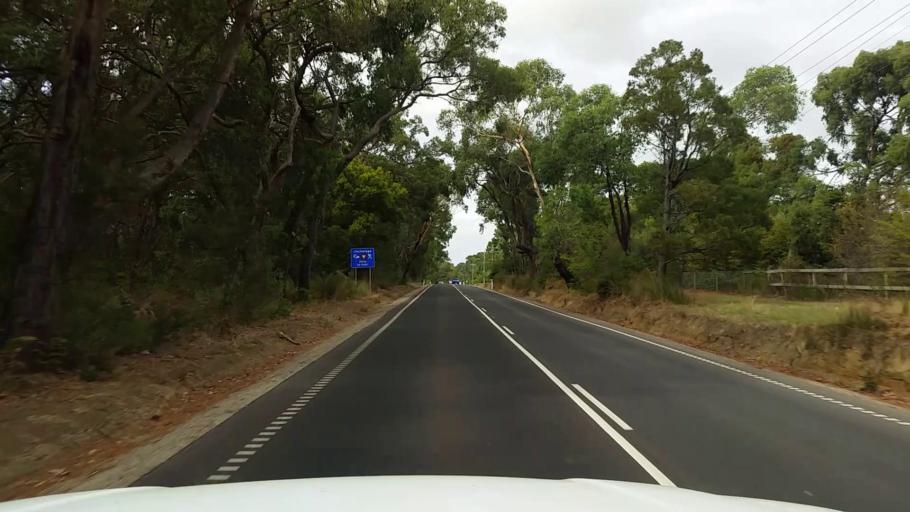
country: AU
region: Victoria
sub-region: Mornington Peninsula
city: Balnarring
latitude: -38.3427
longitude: 145.0998
